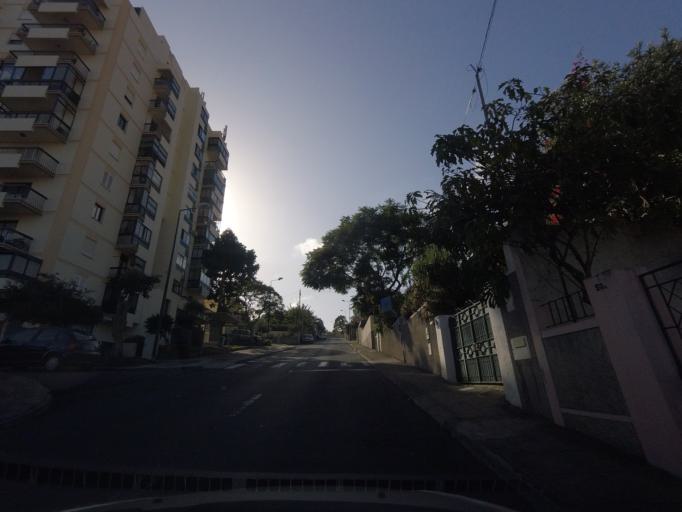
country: PT
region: Madeira
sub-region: Funchal
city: Nossa Senhora do Monte
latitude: 32.6507
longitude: -16.9325
